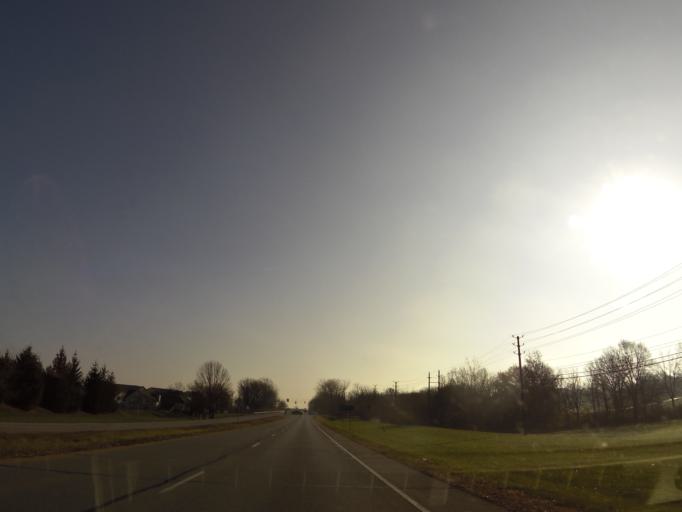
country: US
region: Indiana
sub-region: Marion County
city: Speedway
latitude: 39.8054
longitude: -86.2916
